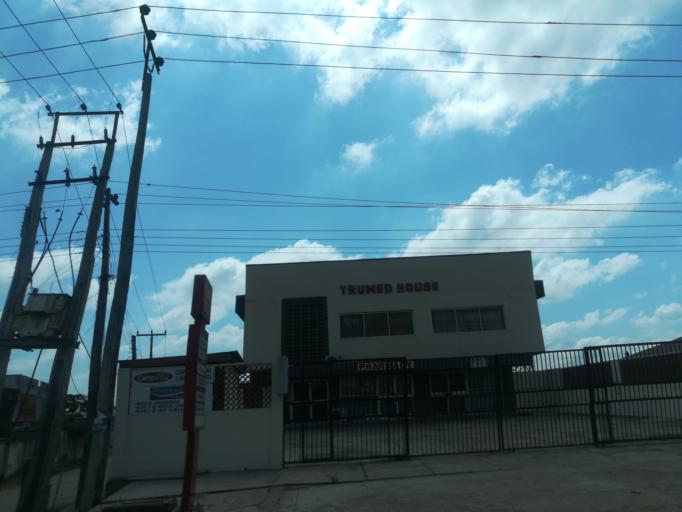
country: NG
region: Oyo
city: Ibadan
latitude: 7.3568
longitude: 3.8670
